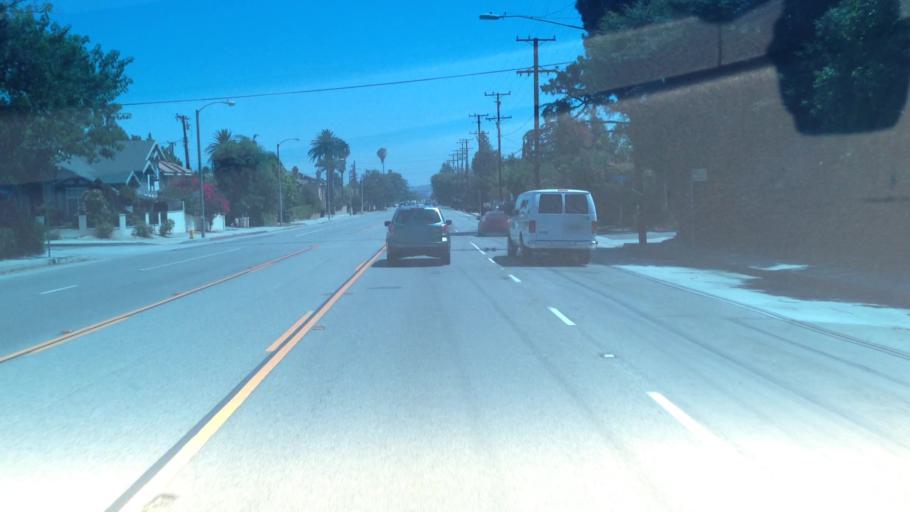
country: US
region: California
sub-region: Los Angeles County
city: San Marino
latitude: 34.1176
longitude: -118.0913
